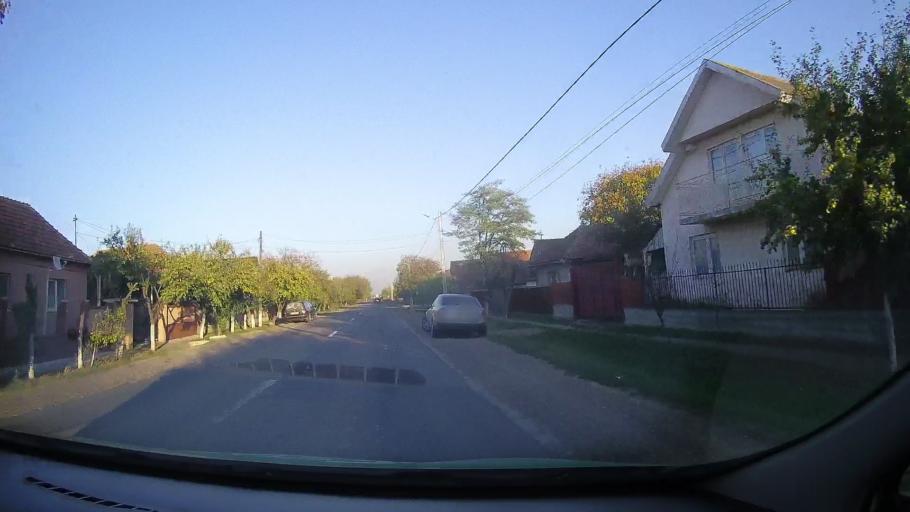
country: RO
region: Bihor
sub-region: Comuna Salard
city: Salard
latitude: 47.2209
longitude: 22.0438
